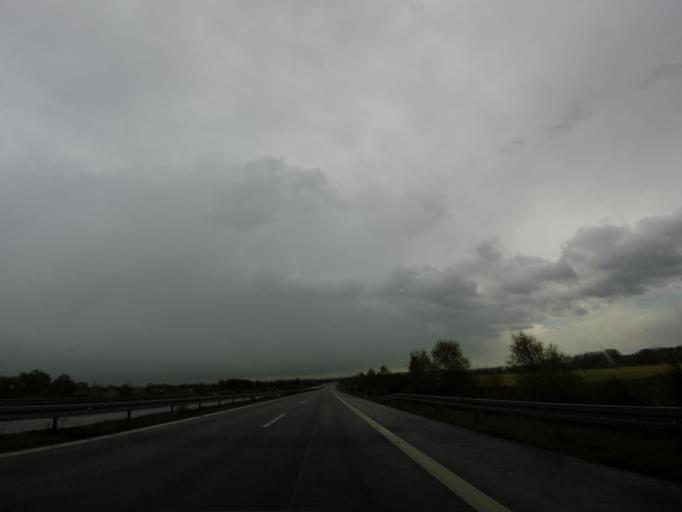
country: DE
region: Lower Saxony
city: Vienenburg
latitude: 51.9375
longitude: 10.6188
